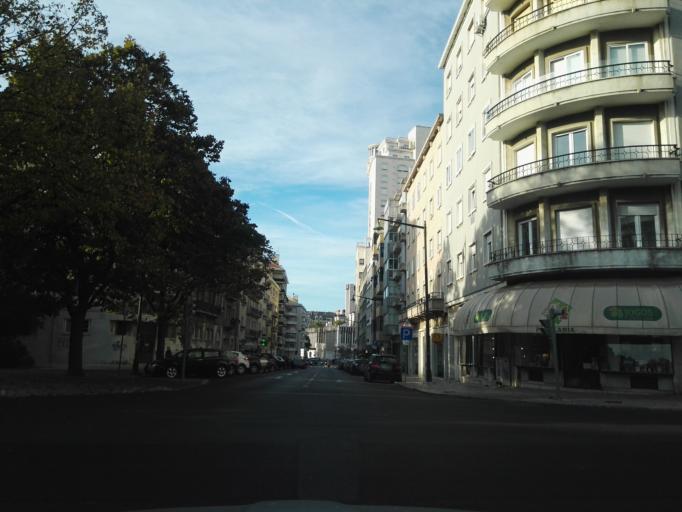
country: PT
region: Lisbon
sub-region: Lisbon
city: Lisbon
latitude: 38.7377
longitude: -9.1421
